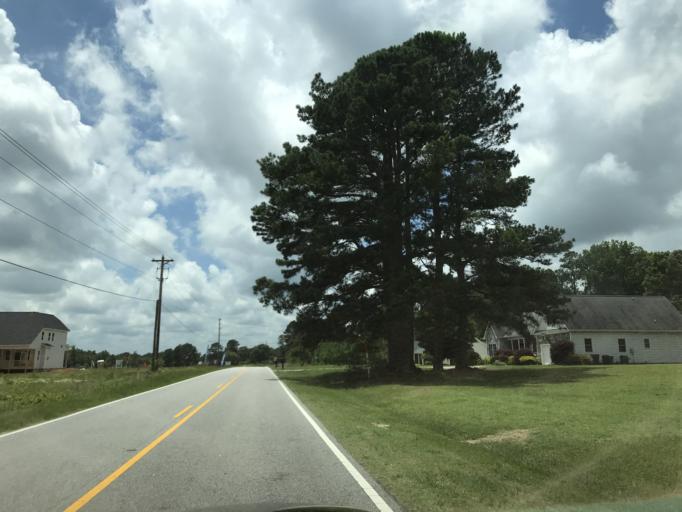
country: US
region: North Carolina
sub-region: Wake County
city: Rolesville
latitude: 35.9519
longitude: -78.3762
